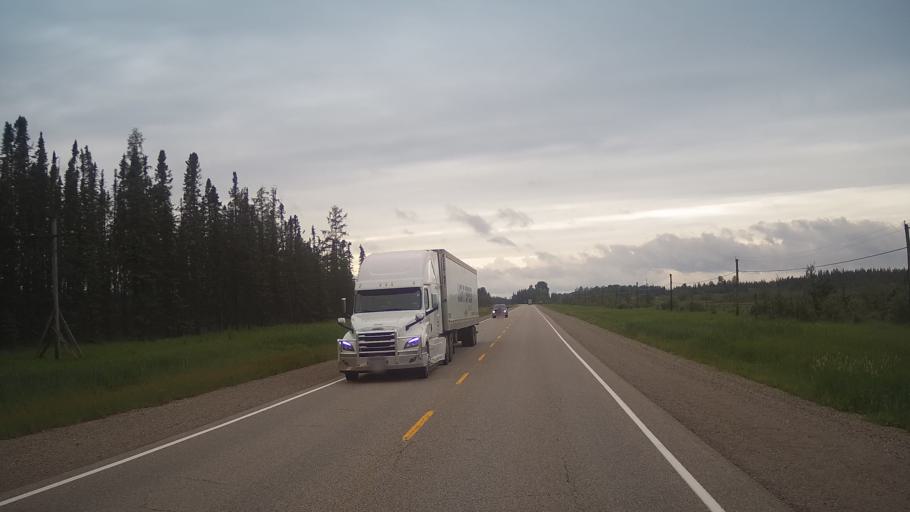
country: CA
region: Ontario
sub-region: Thunder Bay District
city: Thunder Bay
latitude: 48.8808
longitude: -89.9906
